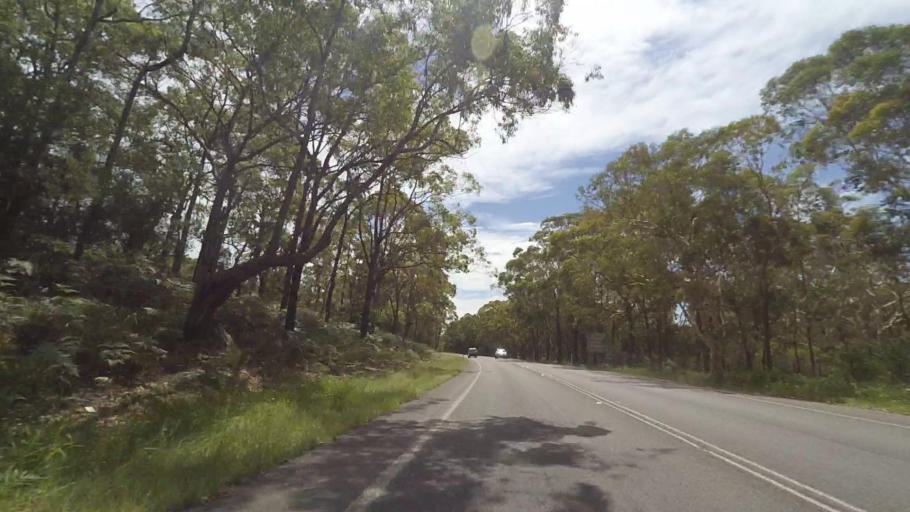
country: AU
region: New South Wales
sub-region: Port Stephens Shire
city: Medowie
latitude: -32.7726
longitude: 151.8660
